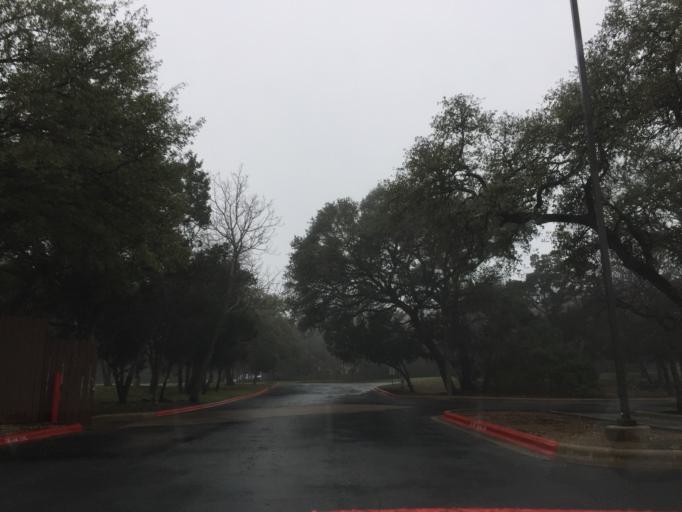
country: US
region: Texas
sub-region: Williamson County
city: Jollyville
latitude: 30.3995
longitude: -97.7331
